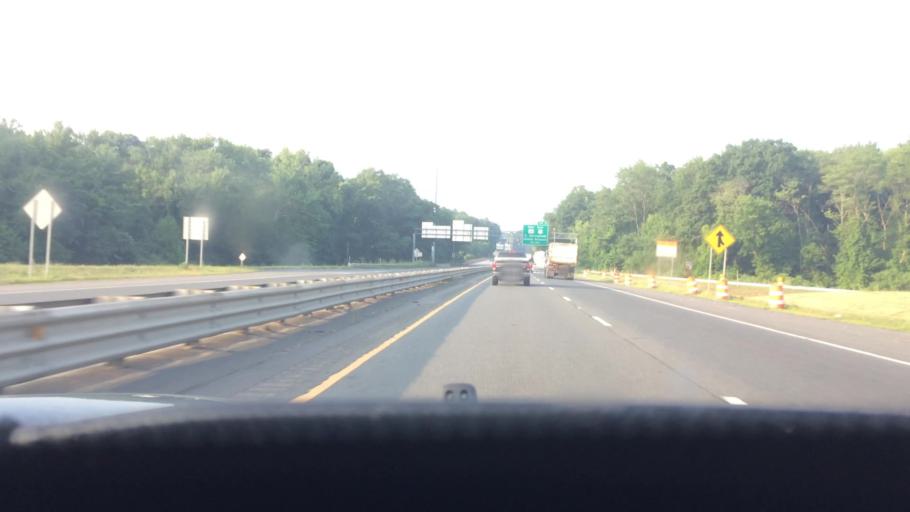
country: US
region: Massachusetts
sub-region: Hampden County
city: North Chicopee
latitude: 42.1614
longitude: -72.5474
